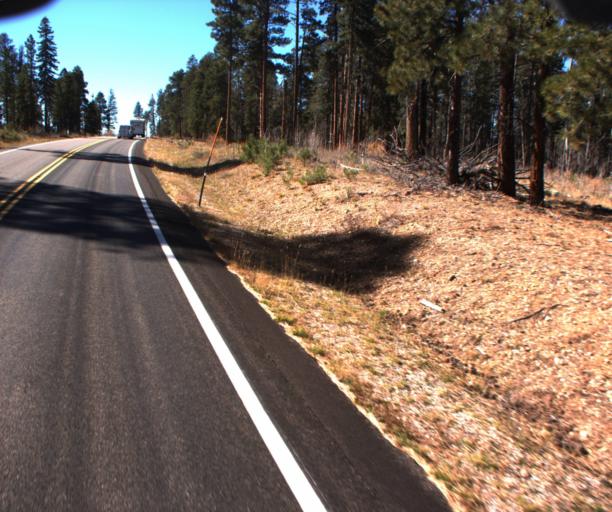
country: US
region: Arizona
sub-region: Coconino County
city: Fredonia
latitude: 36.6277
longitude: -112.1755
